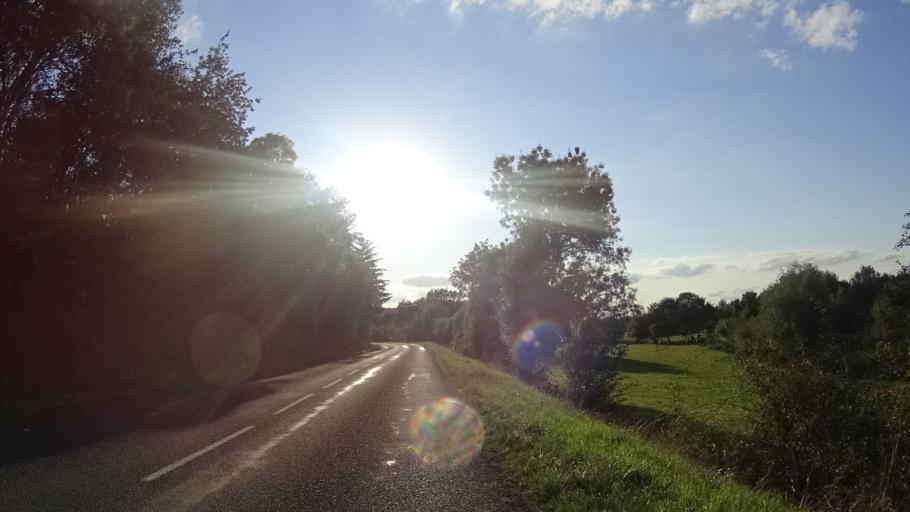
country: FR
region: Pays de la Loire
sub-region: Departement de Maine-et-Loire
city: Champtoceaux
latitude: 47.3397
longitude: -1.2347
